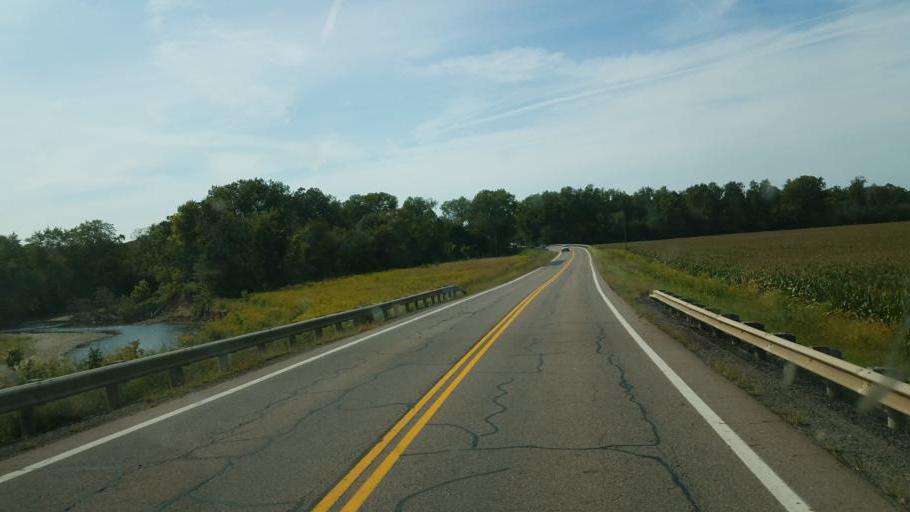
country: US
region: Ohio
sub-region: Knox County
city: Gambier
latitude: 40.3605
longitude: -82.3797
